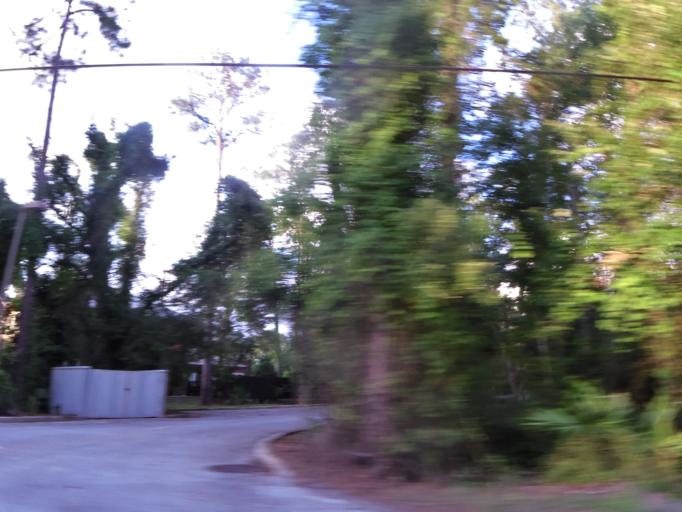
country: US
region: Florida
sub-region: Saint Johns County
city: Fruit Cove
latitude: 30.1373
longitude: -81.6342
